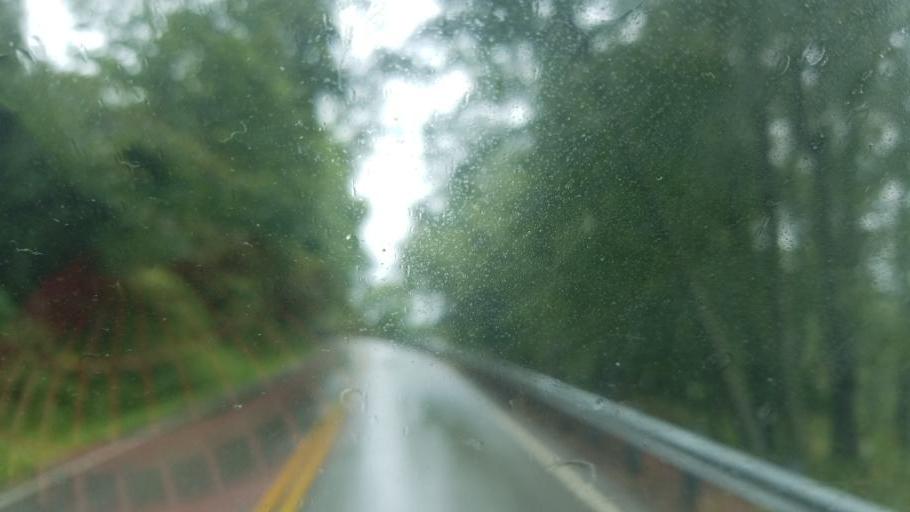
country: US
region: Ohio
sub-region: Scioto County
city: Franklin Furnace
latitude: 38.6593
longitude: -82.9192
